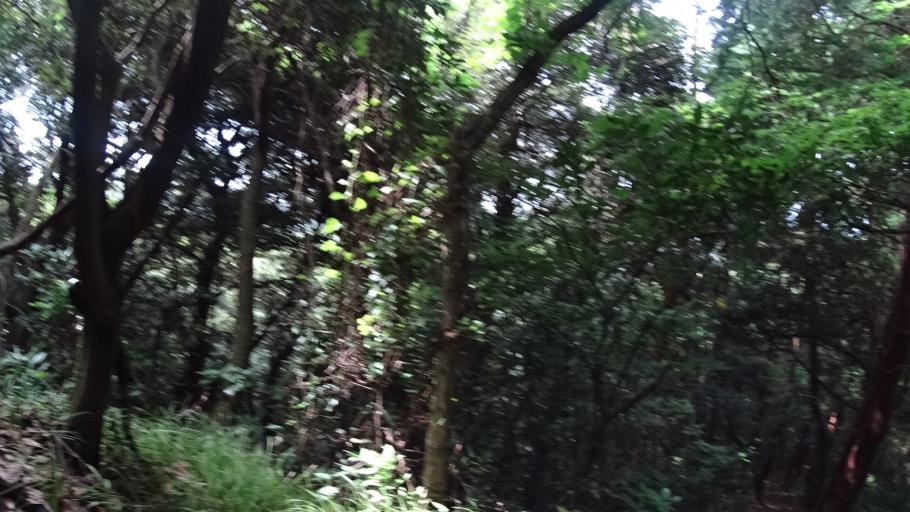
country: JP
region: Kanagawa
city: Yokosuka
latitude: 35.2712
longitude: 139.6333
